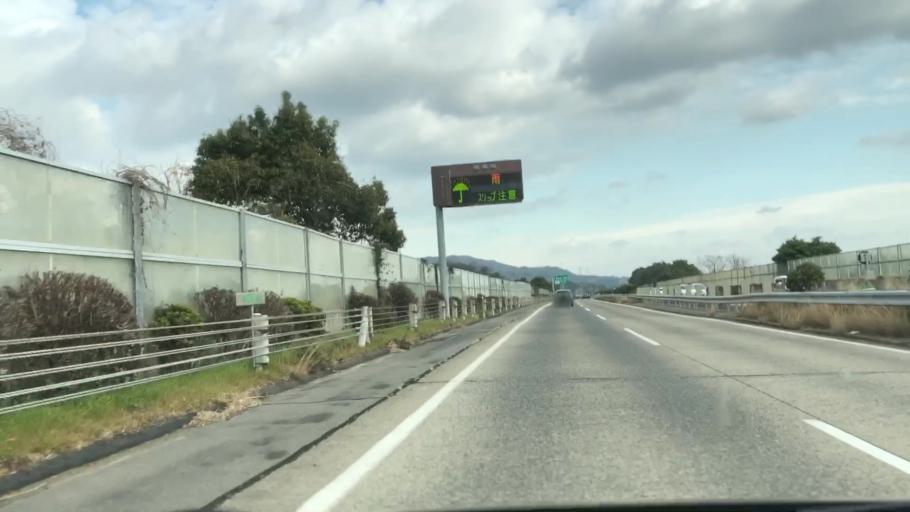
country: JP
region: Saga Prefecture
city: Kanzakimachi-kanzaki
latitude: 33.3531
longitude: 130.3882
